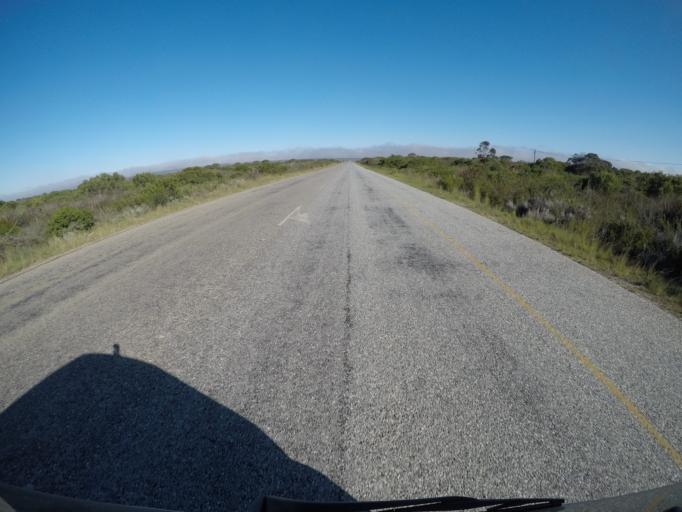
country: ZA
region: Western Cape
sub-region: Eden District Municipality
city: Mossel Bay
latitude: -34.1615
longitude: 22.0100
